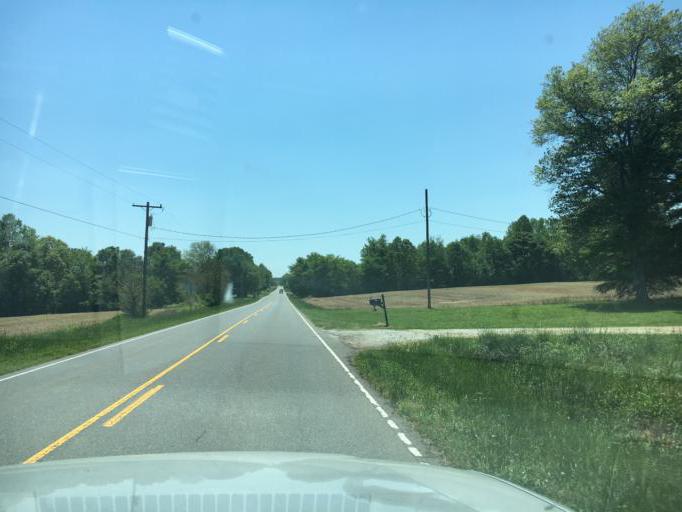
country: US
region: South Carolina
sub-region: Cherokee County
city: Blacksburg
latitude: 35.1983
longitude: -81.5636
